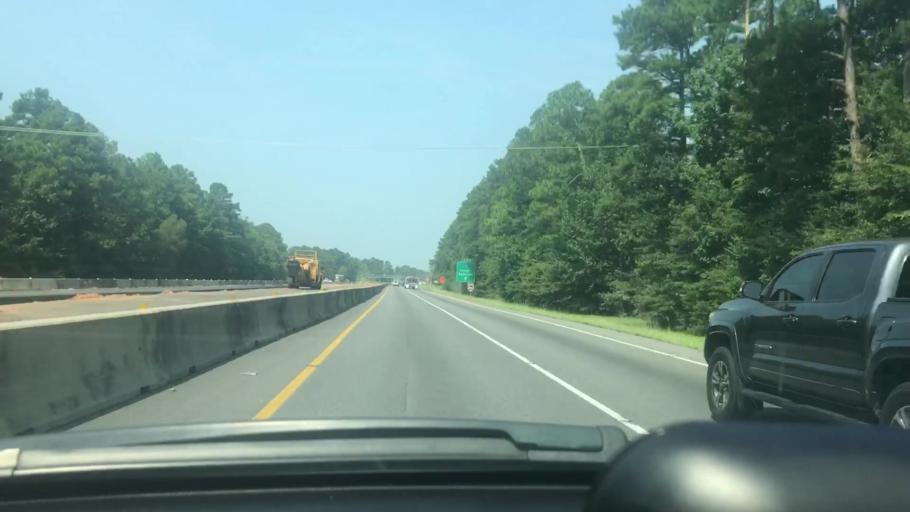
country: US
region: Louisiana
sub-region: Livingston Parish
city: Livingston
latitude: 30.4740
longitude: -90.7900
